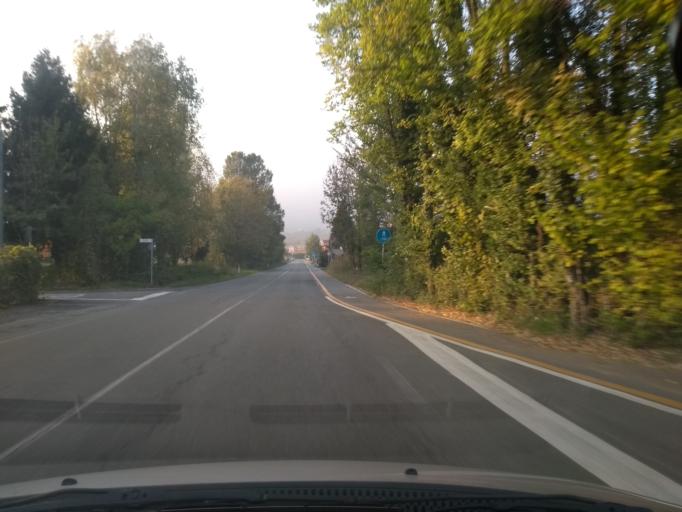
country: IT
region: Piedmont
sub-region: Provincia di Torino
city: Givoletto
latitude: 45.1564
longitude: 7.5028
